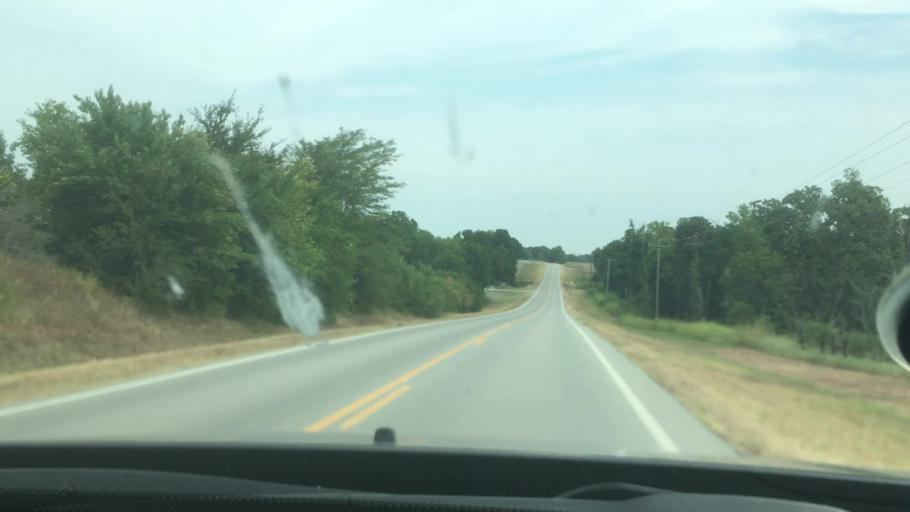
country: US
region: Oklahoma
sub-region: Coal County
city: Coalgate
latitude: 34.5703
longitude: -96.4068
